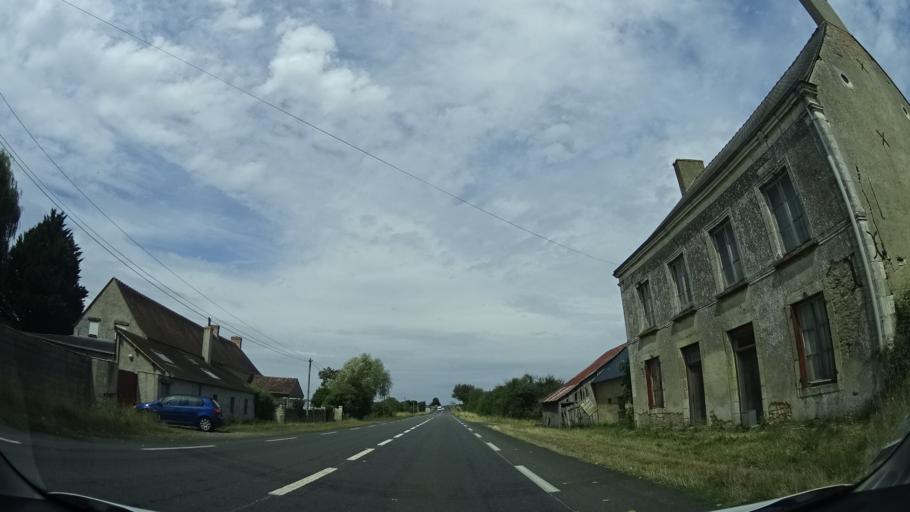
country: FR
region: Pays de la Loire
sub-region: Departement de la Sarthe
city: Vion
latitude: 47.7708
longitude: -0.2036
